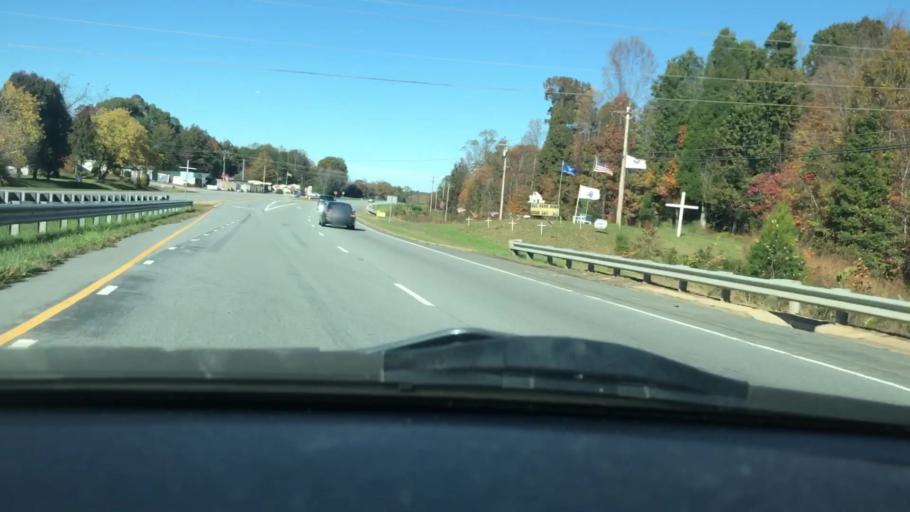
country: US
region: North Carolina
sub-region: Rockingham County
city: Madison
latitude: 36.3296
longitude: -79.9466
